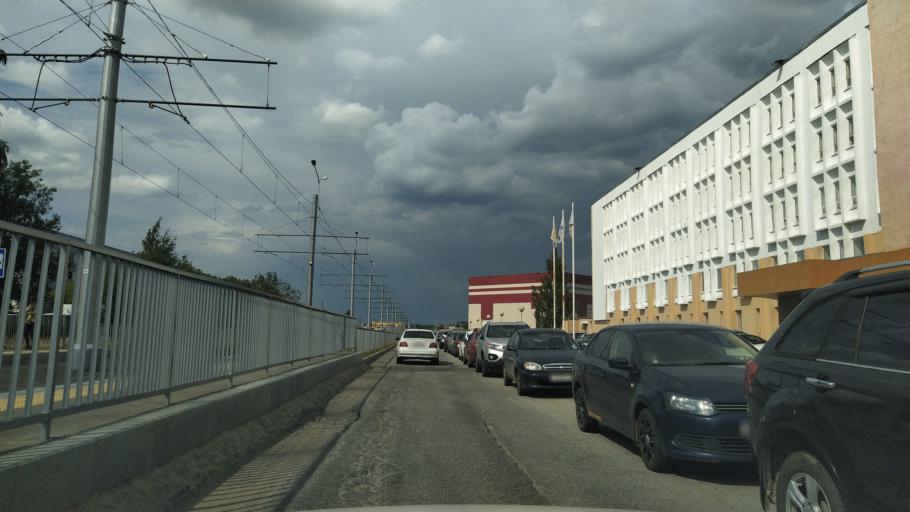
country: RU
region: St.-Petersburg
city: Krasnogvargeisky
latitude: 59.9671
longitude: 30.4631
